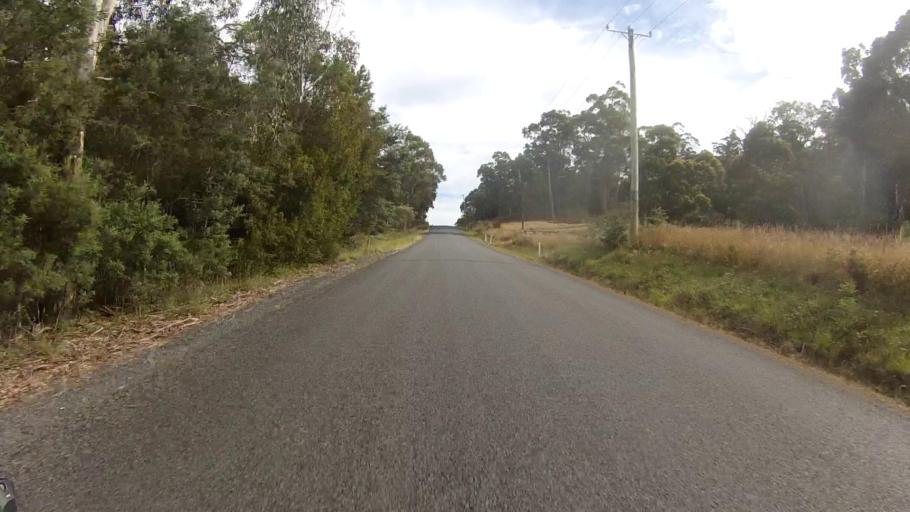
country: AU
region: Tasmania
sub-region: Sorell
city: Sorell
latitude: -42.8029
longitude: 147.7933
